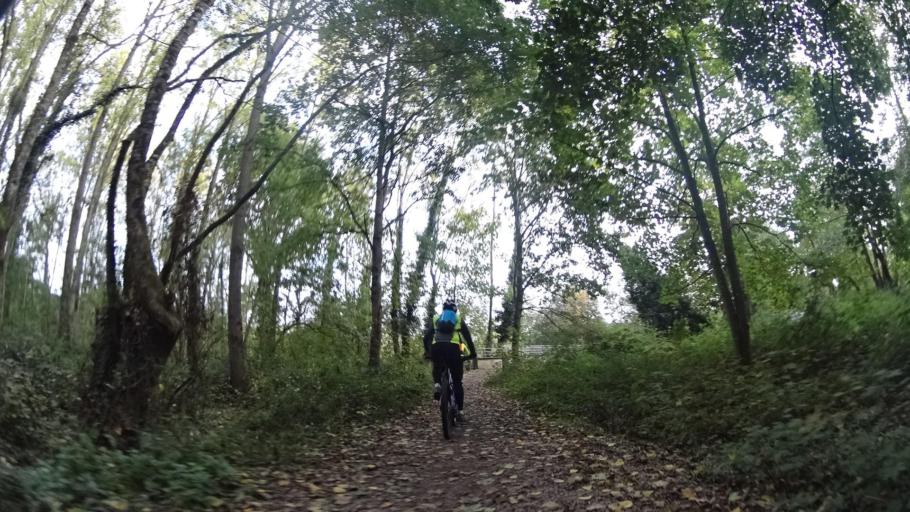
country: FR
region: Brittany
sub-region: Departement des Cotes-d'Armor
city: Evran
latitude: 48.3809
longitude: -1.9935
